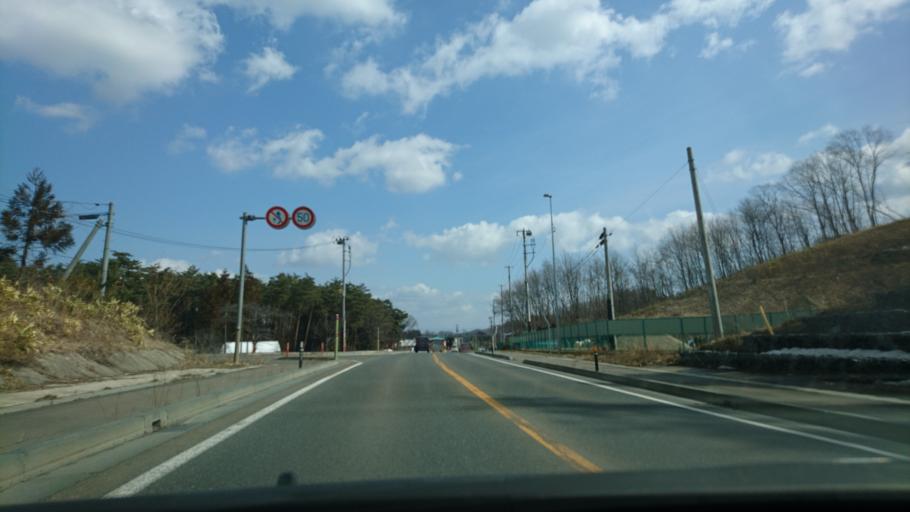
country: JP
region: Iwate
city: Shizukuishi
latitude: 39.6913
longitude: 141.0048
